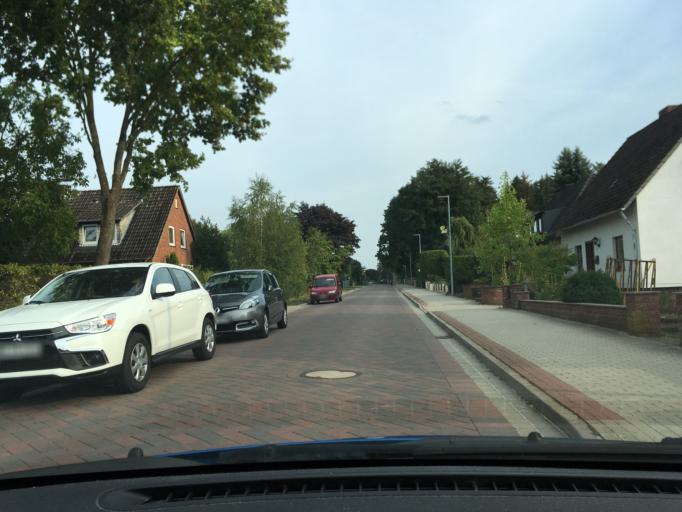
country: DE
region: Lower Saxony
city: Wulfsen
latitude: 53.2919
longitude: 10.1481
